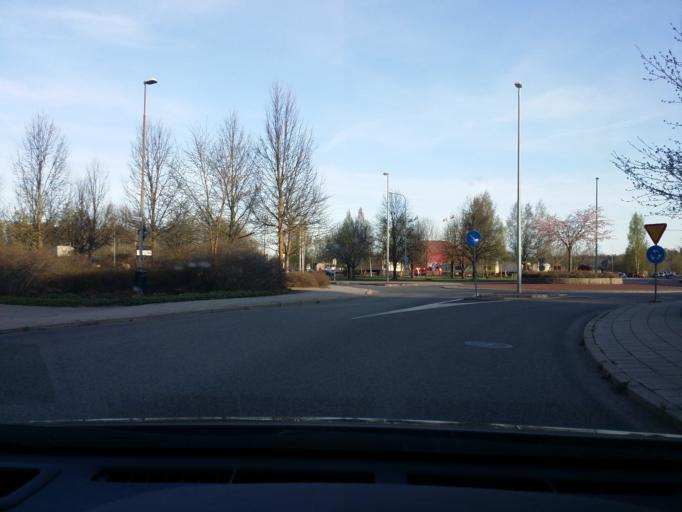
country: SE
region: Dalarna
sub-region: Avesta Kommun
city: Avesta
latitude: 60.1410
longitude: 16.1685
